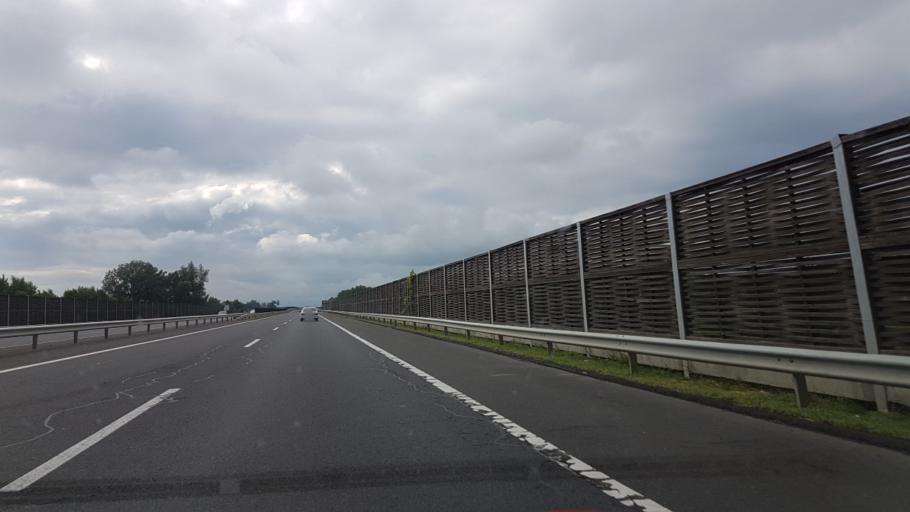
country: HU
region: Hajdu-Bihar
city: Polgar
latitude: 47.8530
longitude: 21.0586
